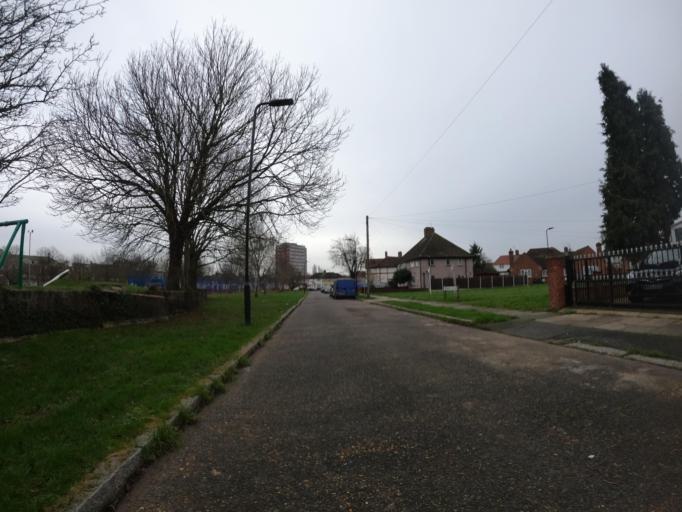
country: GB
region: England
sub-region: Greater London
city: Southall
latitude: 51.5173
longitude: -0.3617
